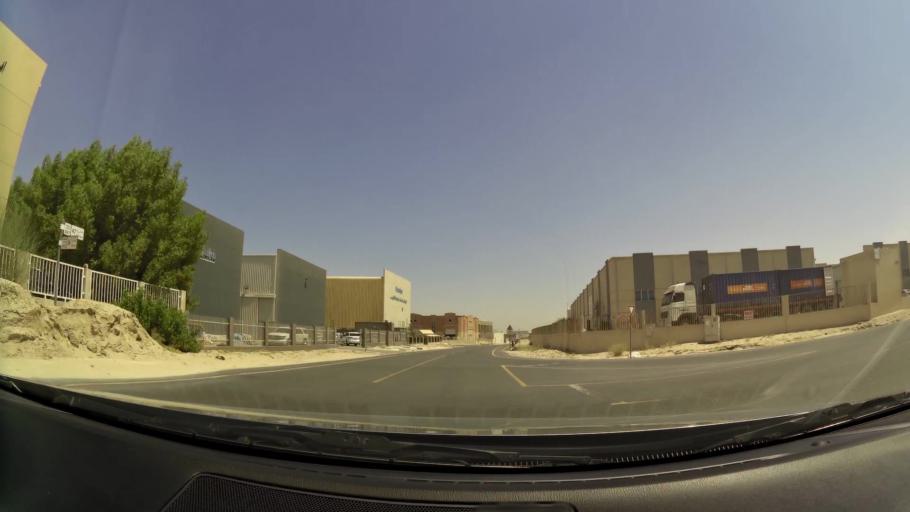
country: AE
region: Dubai
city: Dubai
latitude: 24.9739
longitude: 55.1896
